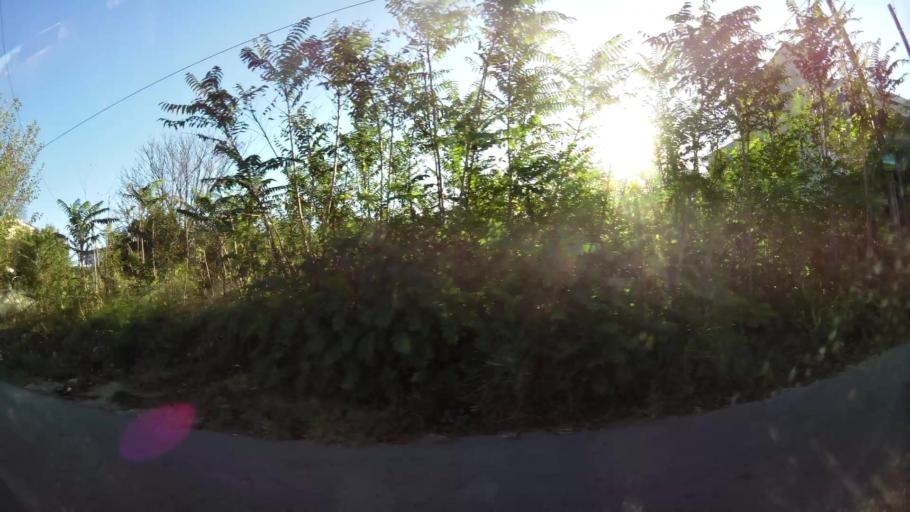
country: GR
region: Attica
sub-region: Nomarchia Anatolikis Attikis
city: Pallini
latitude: 38.0107
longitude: 23.8731
